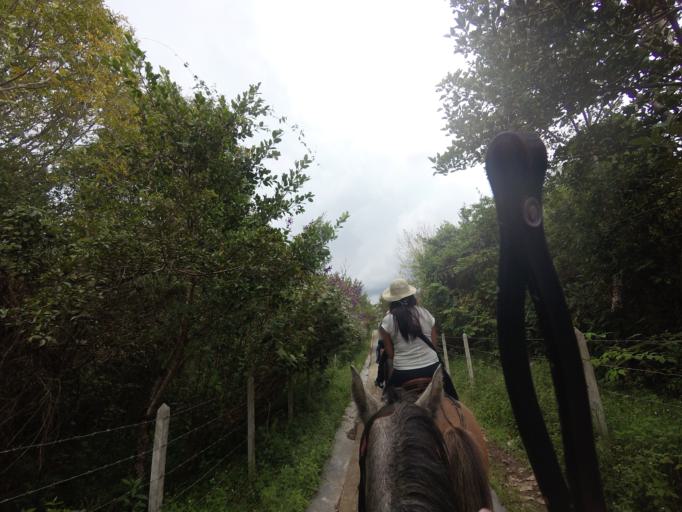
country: CO
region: Huila
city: San Agustin
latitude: 1.8889
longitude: -76.2942
